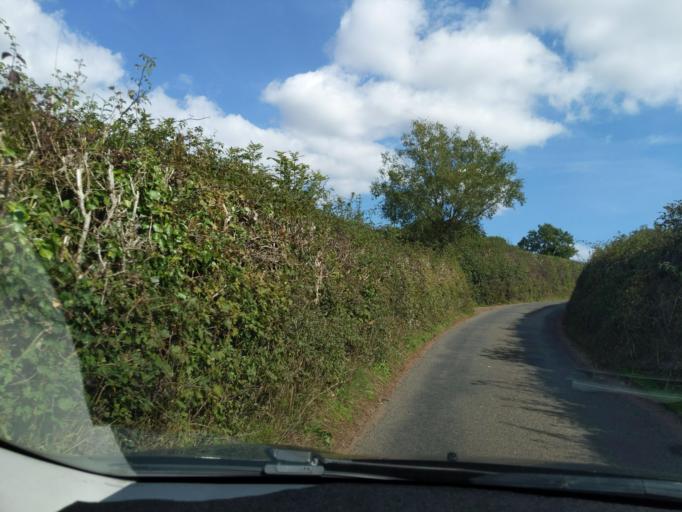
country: GB
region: England
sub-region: Devon
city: Marldon
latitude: 50.4621
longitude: -3.6203
